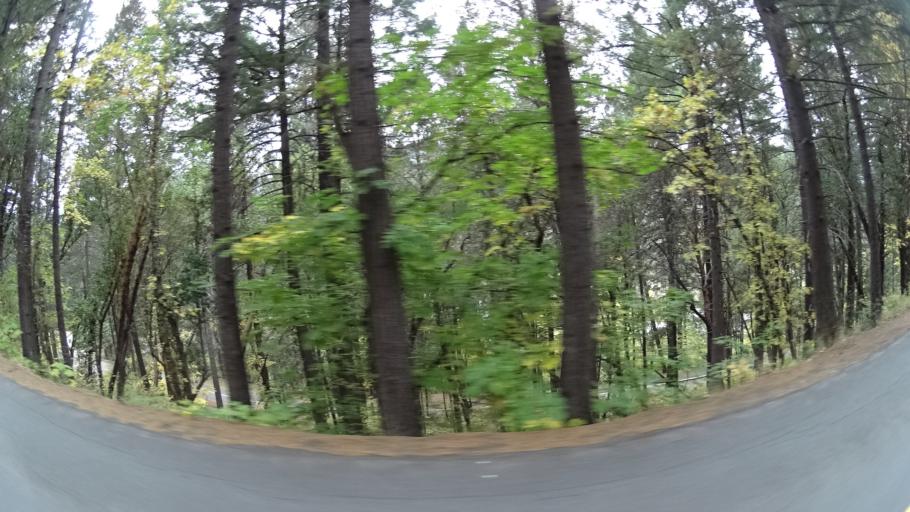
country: US
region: California
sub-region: Siskiyou County
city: Happy Camp
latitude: 41.7857
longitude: -123.3862
